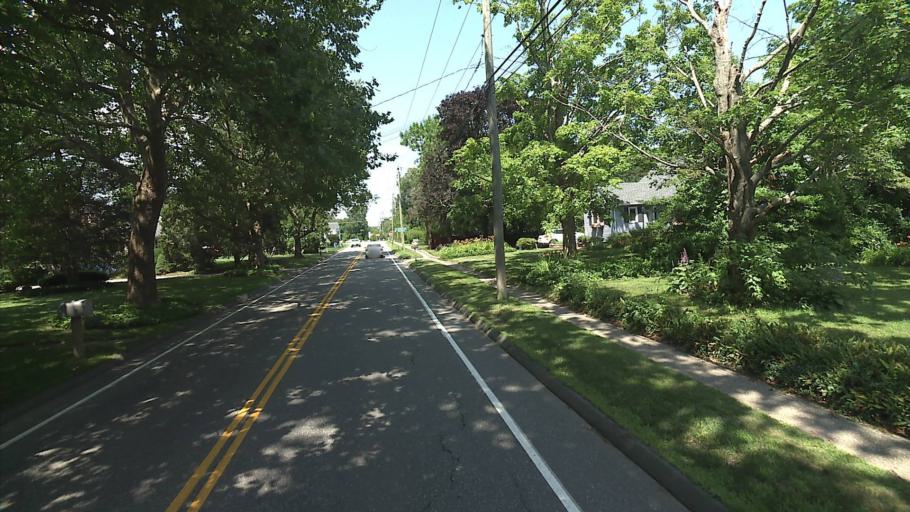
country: US
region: Connecticut
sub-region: Middlesex County
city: Saybrook Manor
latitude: 41.2859
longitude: -72.3901
